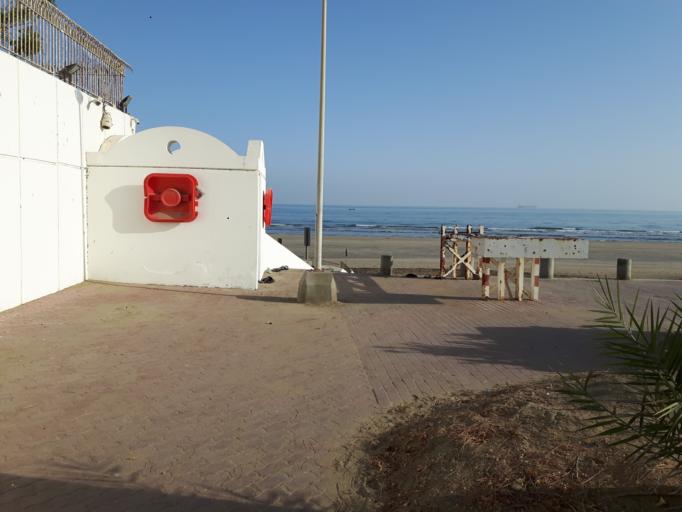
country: OM
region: Muhafazat Masqat
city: Bawshar
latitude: 23.6086
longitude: 58.4390
